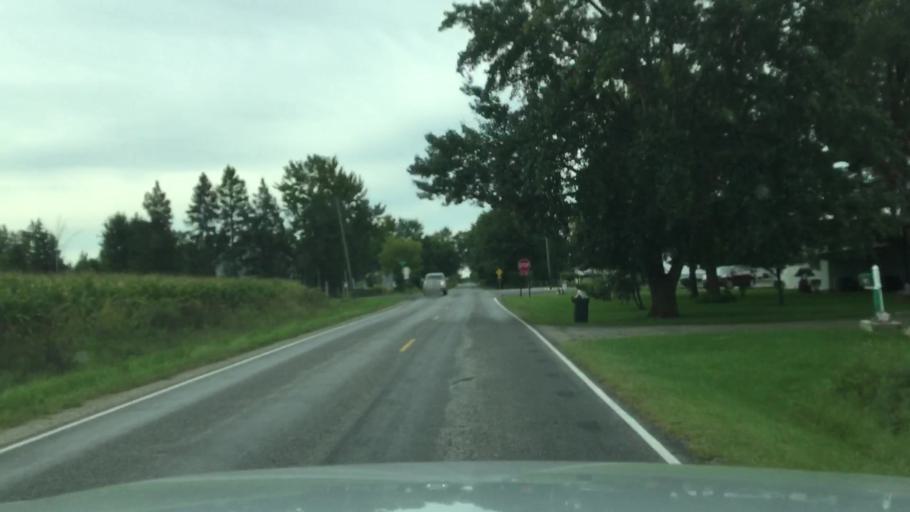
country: US
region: Michigan
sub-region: Genesee County
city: Flushing
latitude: 43.0594
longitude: -83.9876
